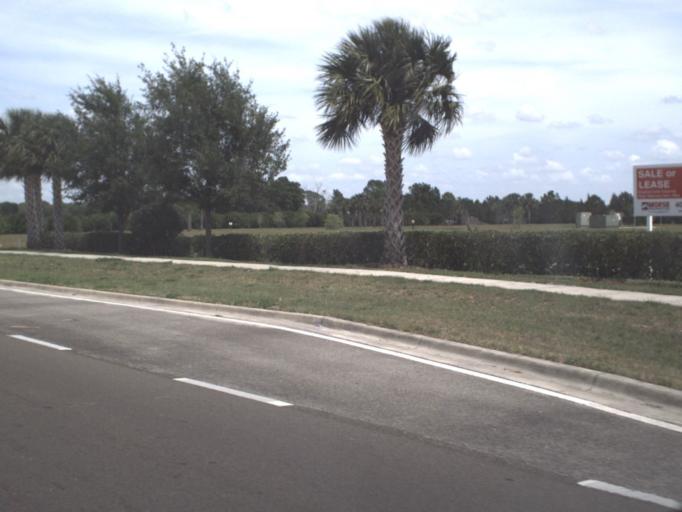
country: US
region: Florida
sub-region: Lake County
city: Mount Dora
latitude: 28.8261
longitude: -81.6438
